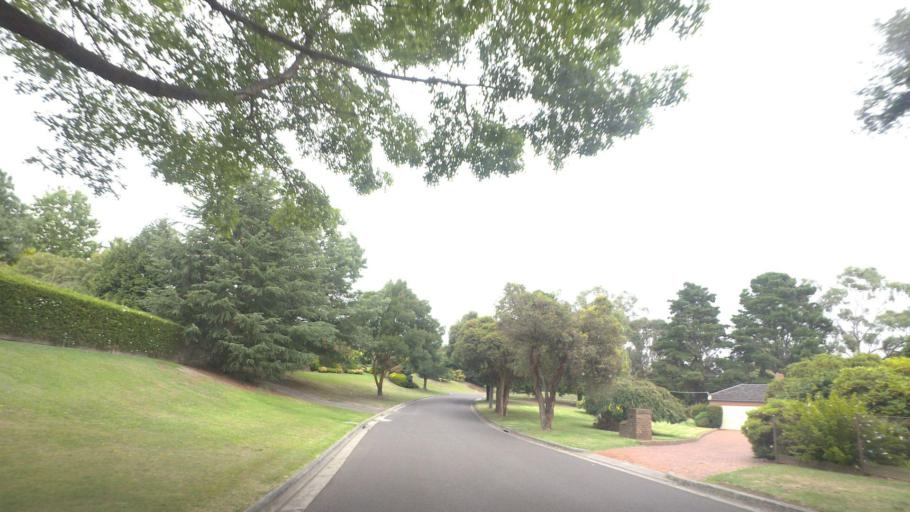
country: AU
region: Victoria
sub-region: Yarra Ranges
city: Lilydale
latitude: -37.7778
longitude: 145.3450
